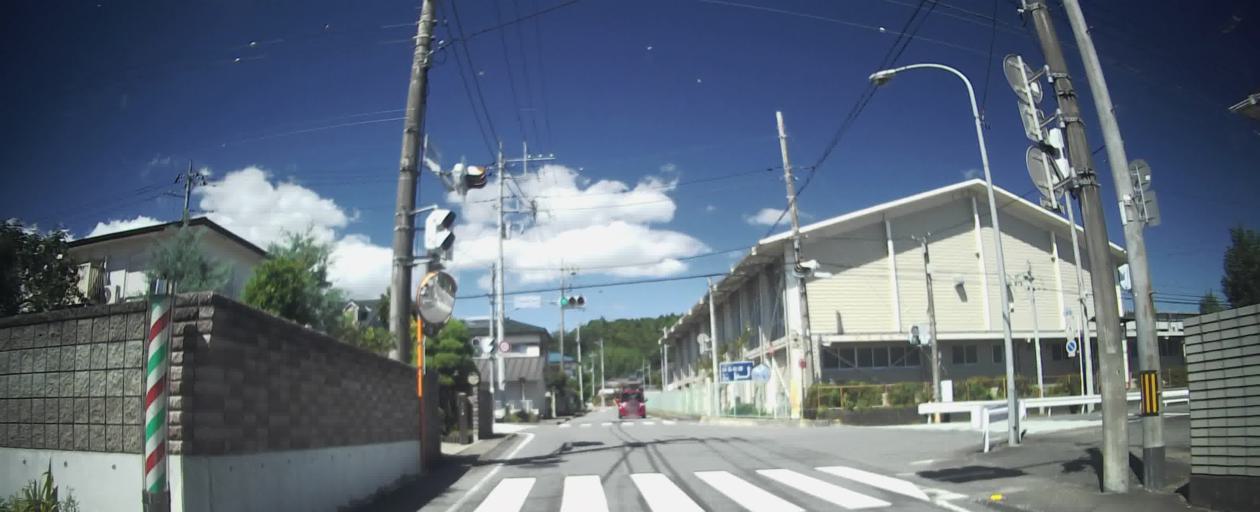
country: JP
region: Gunma
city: Kanekomachi
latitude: 36.3979
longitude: 138.9545
